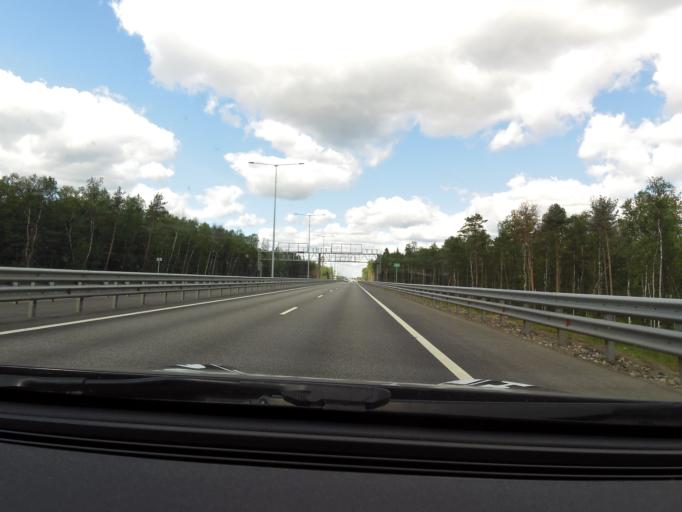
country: RU
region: Tverskaya
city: Krasnomayskiy
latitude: 57.4577
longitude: 34.3931
